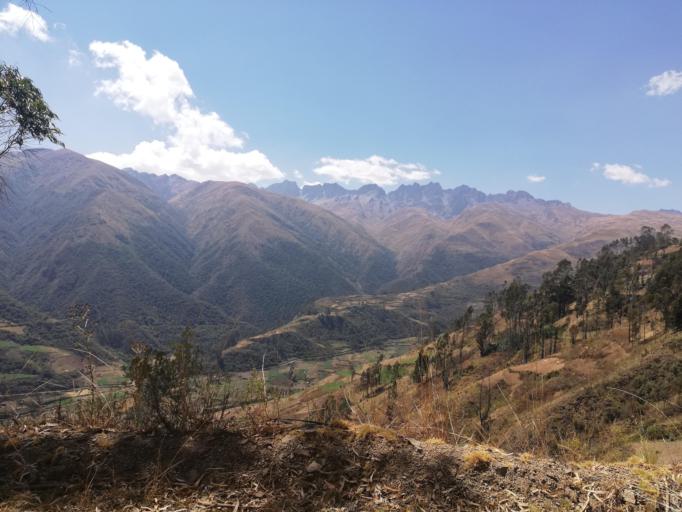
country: BO
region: Cochabamba
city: Colchani
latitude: -17.2242
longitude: -66.5212
